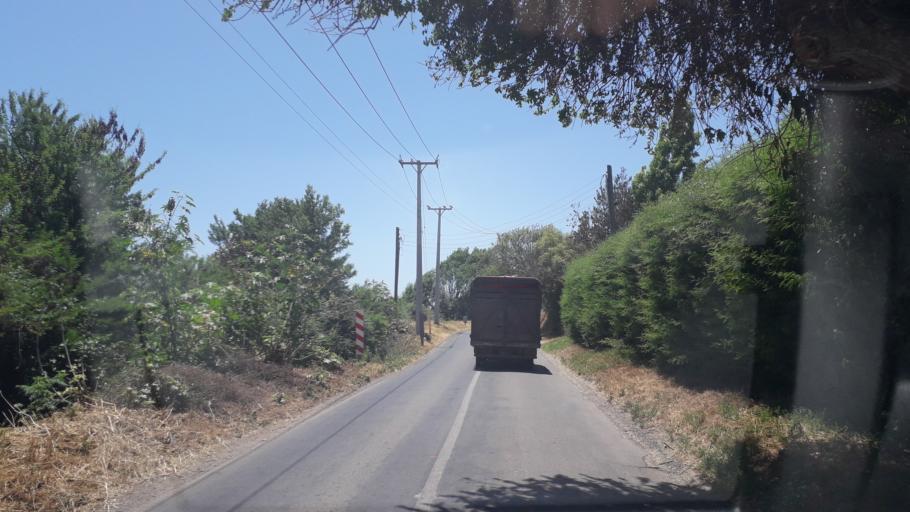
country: CL
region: Valparaiso
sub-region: Provincia de Quillota
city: Quillota
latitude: -32.9329
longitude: -71.2633
